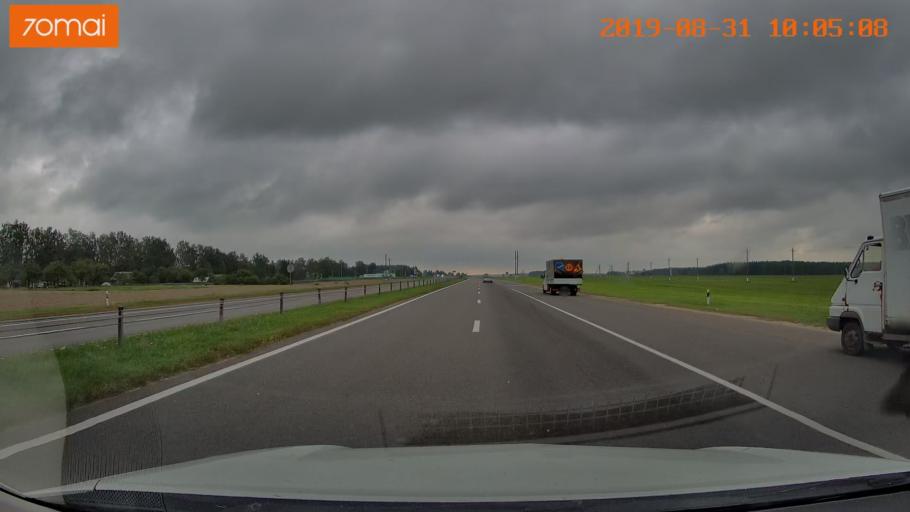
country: BY
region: Mogilev
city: Buynichy
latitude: 53.9667
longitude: 30.1623
